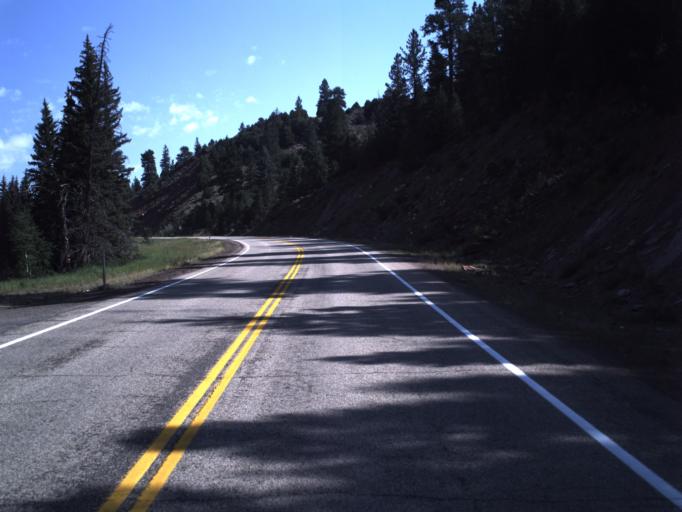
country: US
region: Utah
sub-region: Daggett County
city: Manila
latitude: 40.8743
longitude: -109.6923
